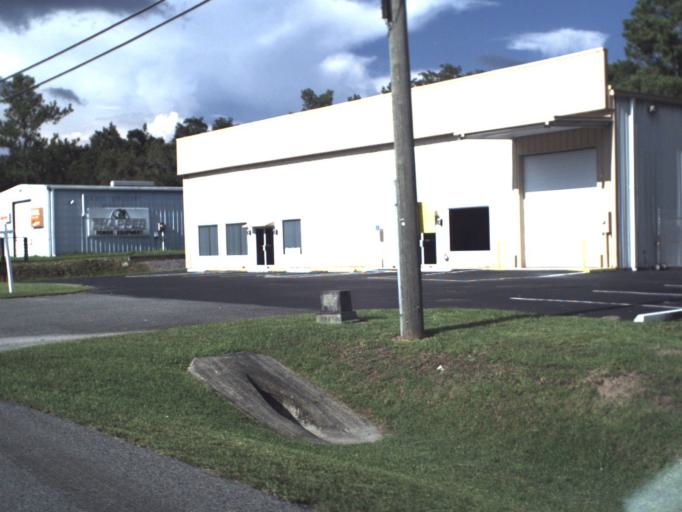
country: US
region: Florida
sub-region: Hernando County
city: Brooksville
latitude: 28.5599
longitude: -82.3976
